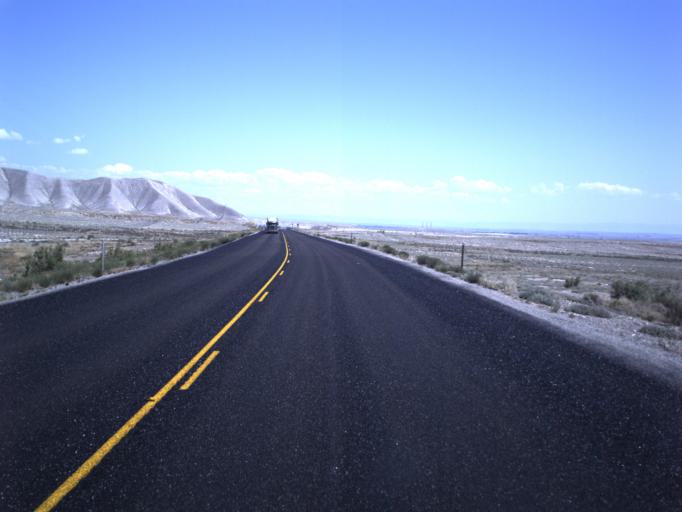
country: US
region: Utah
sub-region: Emery County
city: Ferron
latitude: 39.0290
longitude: -111.1312
